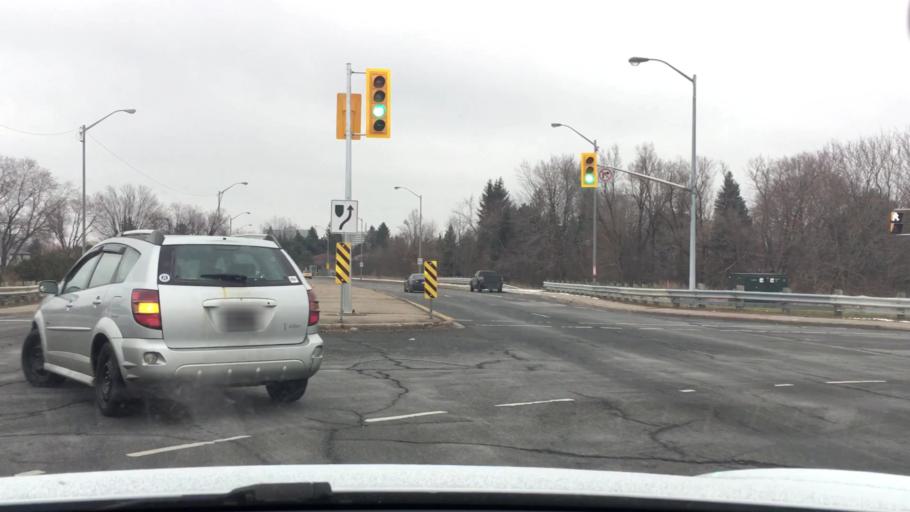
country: CA
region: Ontario
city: Scarborough
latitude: 43.7949
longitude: -79.2161
